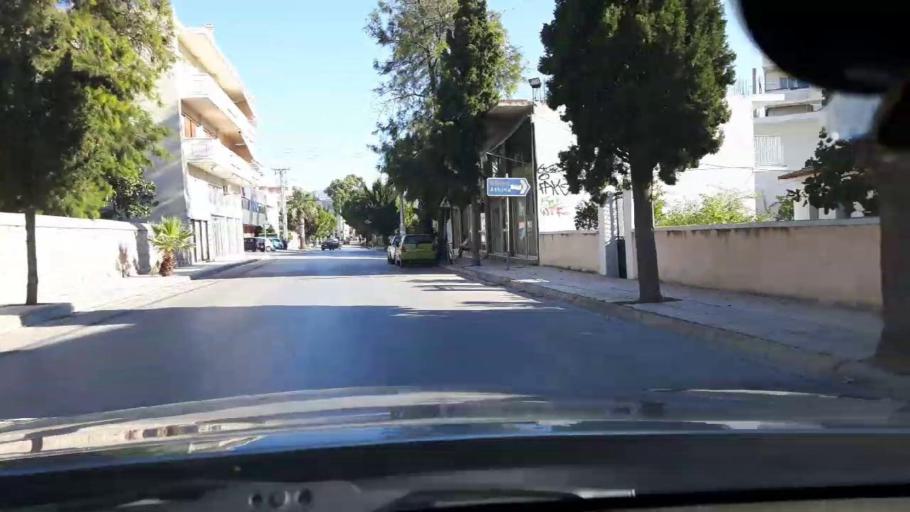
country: GR
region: Attica
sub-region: Nomarchia Anatolikis Attikis
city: Markopoulo
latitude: 37.8794
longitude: 23.9337
